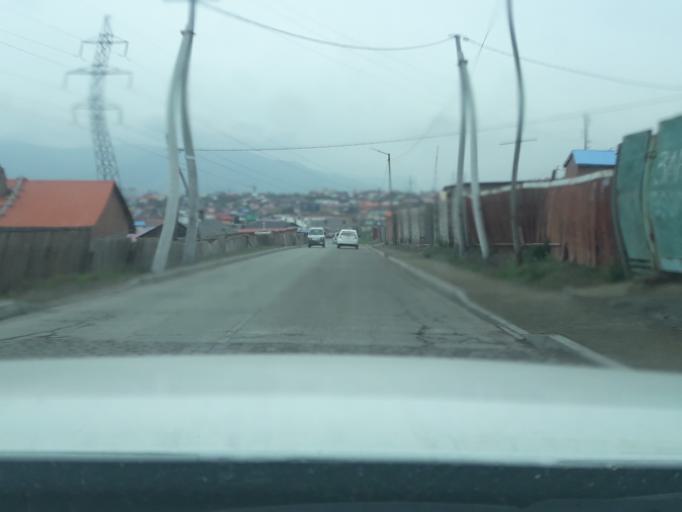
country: MN
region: Ulaanbaatar
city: Ulaanbaatar
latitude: 47.9492
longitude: 106.9048
